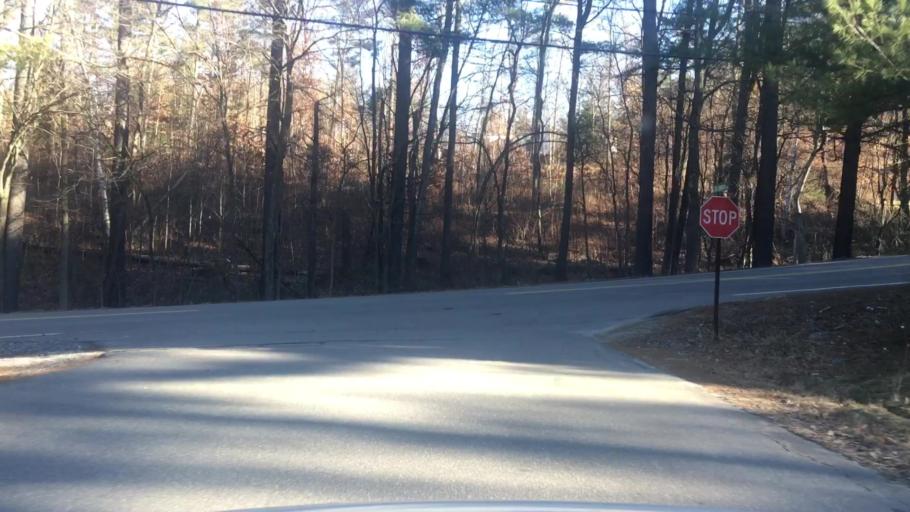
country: US
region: New Hampshire
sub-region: Rockingham County
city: Londonderry
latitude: 42.8899
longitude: -71.4098
